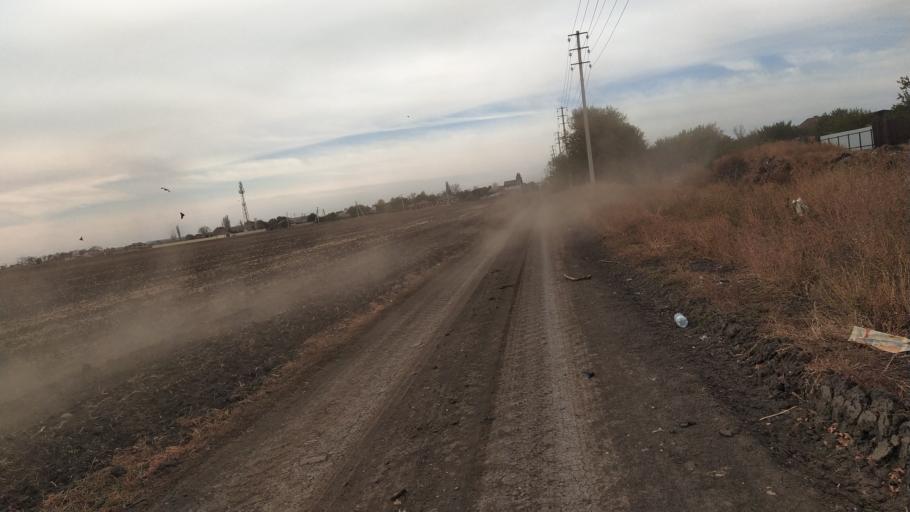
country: RU
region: Rostov
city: Bataysk
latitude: 47.1101
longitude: 39.6828
